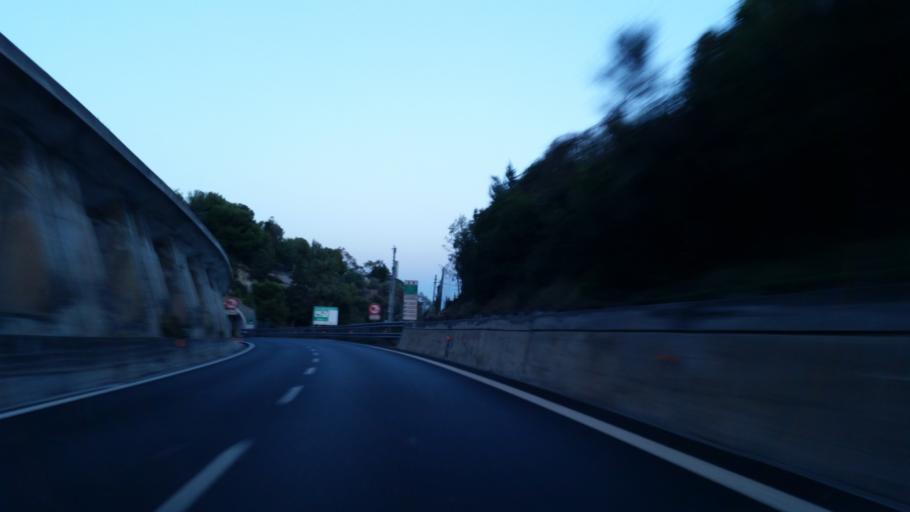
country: FR
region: Provence-Alpes-Cote d'Azur
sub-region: Departement des Alpes-Maritimes
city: Menton
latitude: 43.7871
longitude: 7.5508
